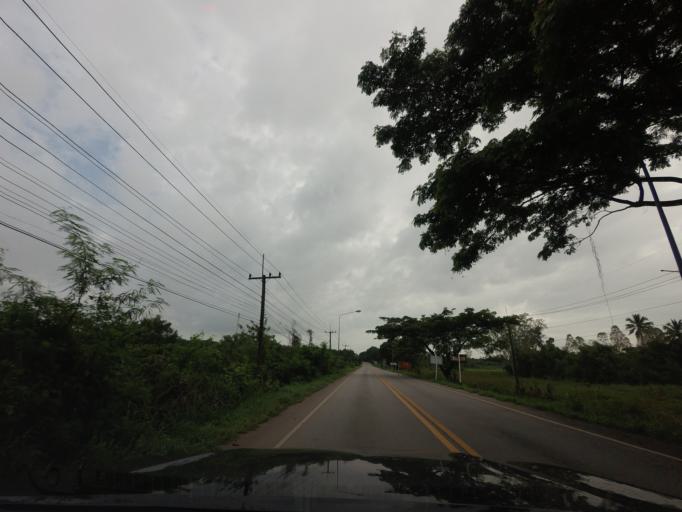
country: TH
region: Changwat Udon Thani
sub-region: Amphoe Ban Phue
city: Ban Phue
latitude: 17.7193
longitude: 102.3919
